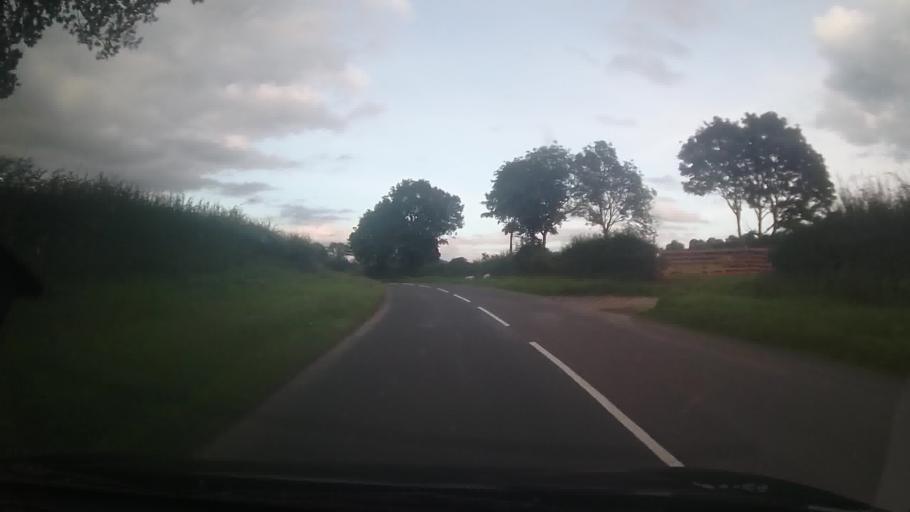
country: GB
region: Wales
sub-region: Sir Powys
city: Llanrhaeadr-ym-Mochnant
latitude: 52.8092
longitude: -3.3177
